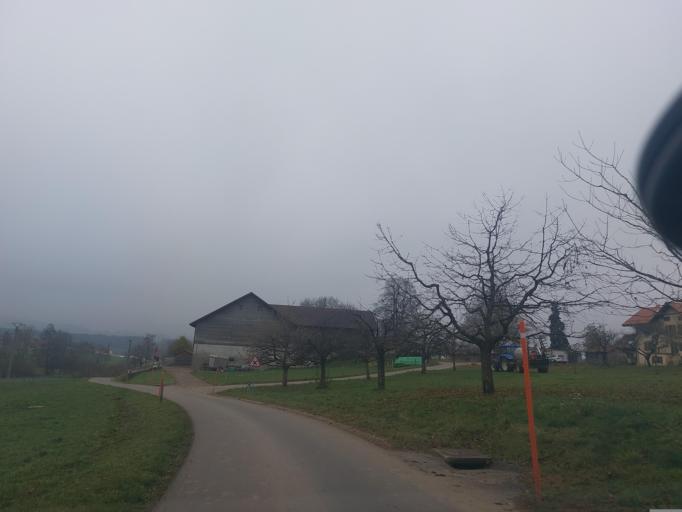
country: CH
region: Vaud
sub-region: Lavaux-Oron District
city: Palezieux
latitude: 46.5547
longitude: 6.8518
